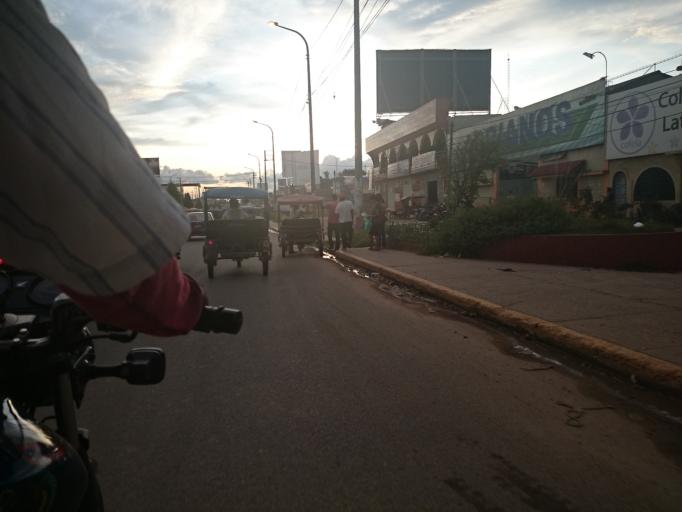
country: PE
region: Ucayali
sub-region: Provincia de Coronel Portillo
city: Pucallpa
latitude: -8.3832
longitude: -74.5432
